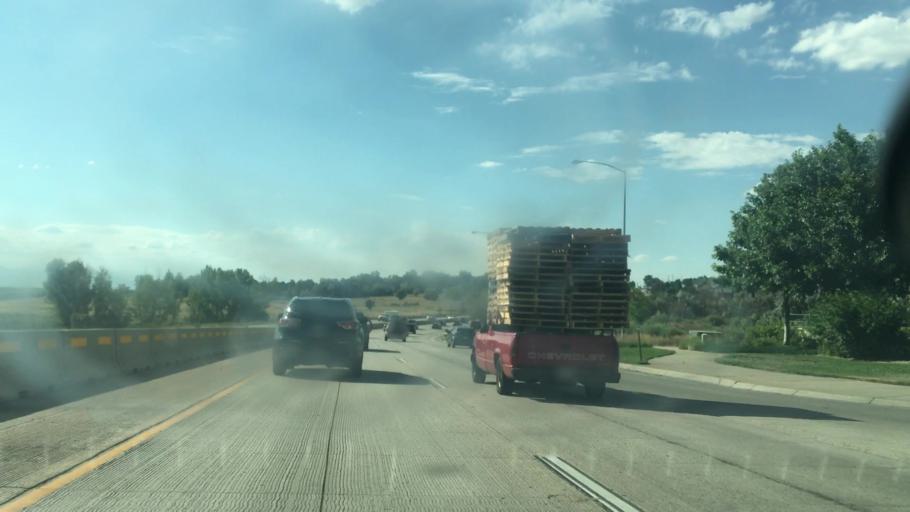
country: US
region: Colorado
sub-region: Arapahoe County
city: Dove Valley
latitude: 39.6172
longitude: -104.8182
